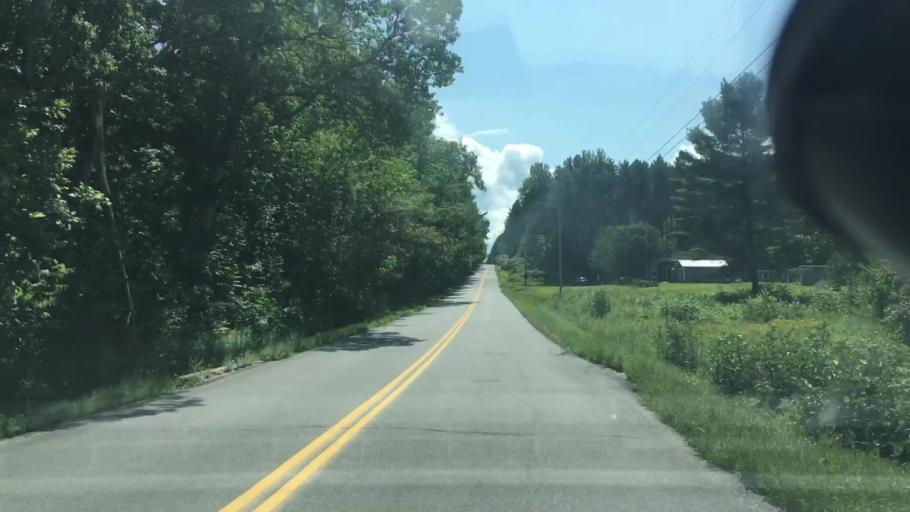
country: US
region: Maine
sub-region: Somerset County
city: Skowhegan
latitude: 44.7033
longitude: -69.6957
